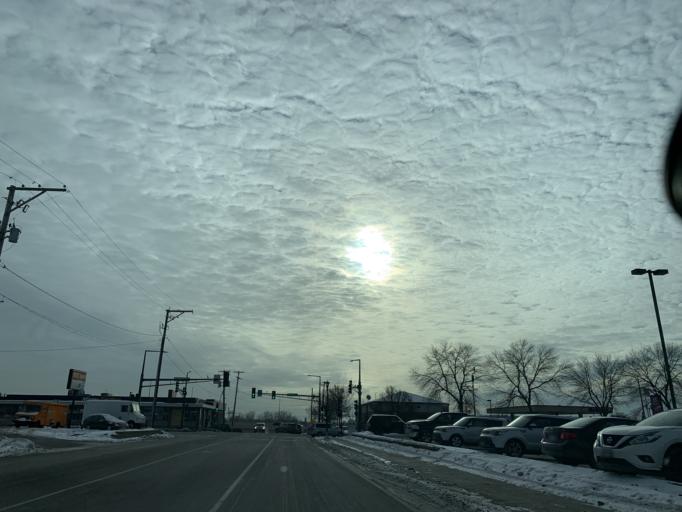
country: US
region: Minnesota
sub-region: Ramsey County
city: Saint Paul
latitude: 44.9553
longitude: -93.0813
